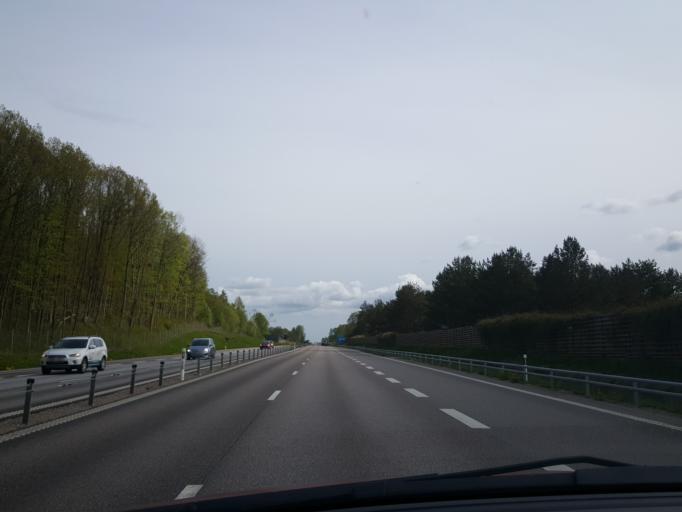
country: SE
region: Vaestra Goetaland
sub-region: Lilla Edets Kommun
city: Lilla Edet
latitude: 58.1413
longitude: 12.1355
